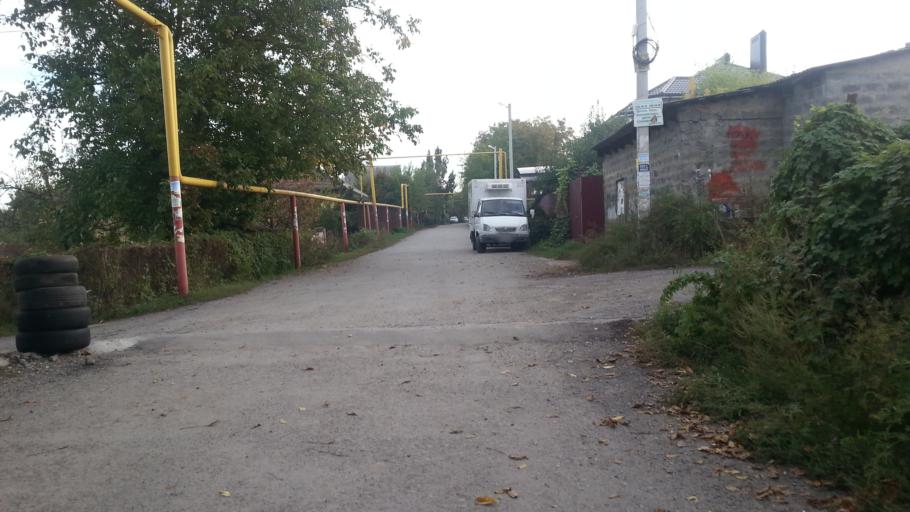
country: RU
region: Rostov
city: Severnyy
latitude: 47.2907
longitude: 39.6702
